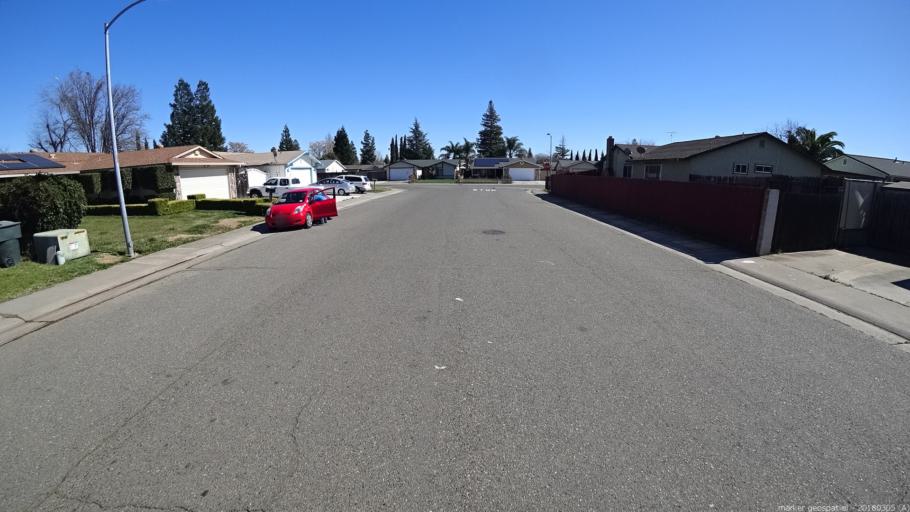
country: US
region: California
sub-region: Sacramento County
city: Florin
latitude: 38.4936
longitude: -121.3874
